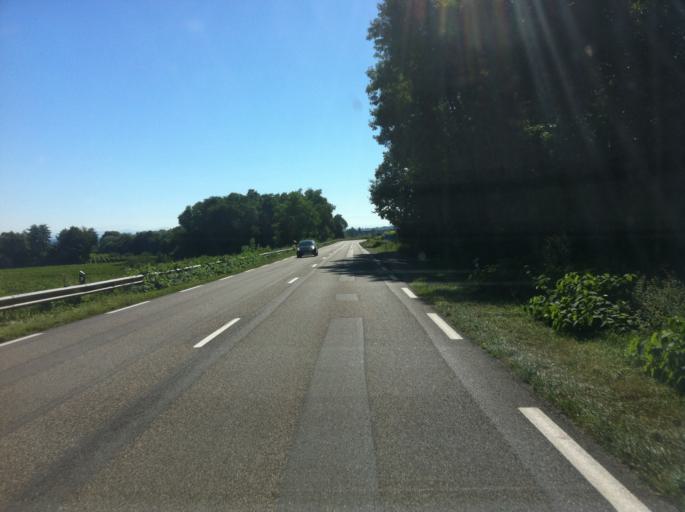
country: FR
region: Alsace
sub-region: Departement du Haut-Rhin
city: Kaysersberg
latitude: 48.1339
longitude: 7.2746
